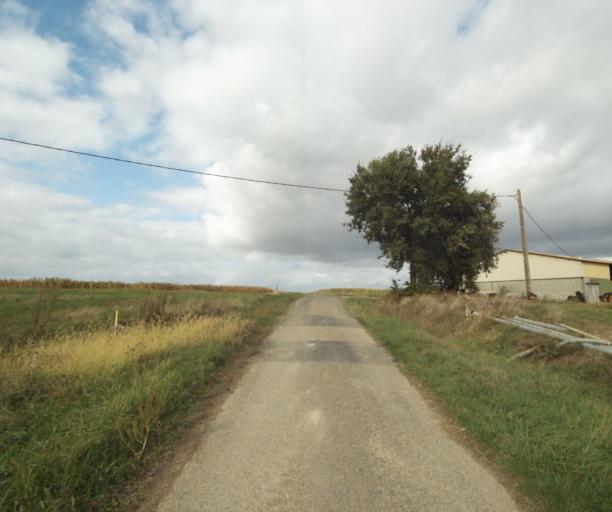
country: FR
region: Midi-Pyrenees
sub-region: Departement du Tarn-et-Garonne
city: Beaumont-de-Lomagne
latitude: 43.9001
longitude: 1.1027
